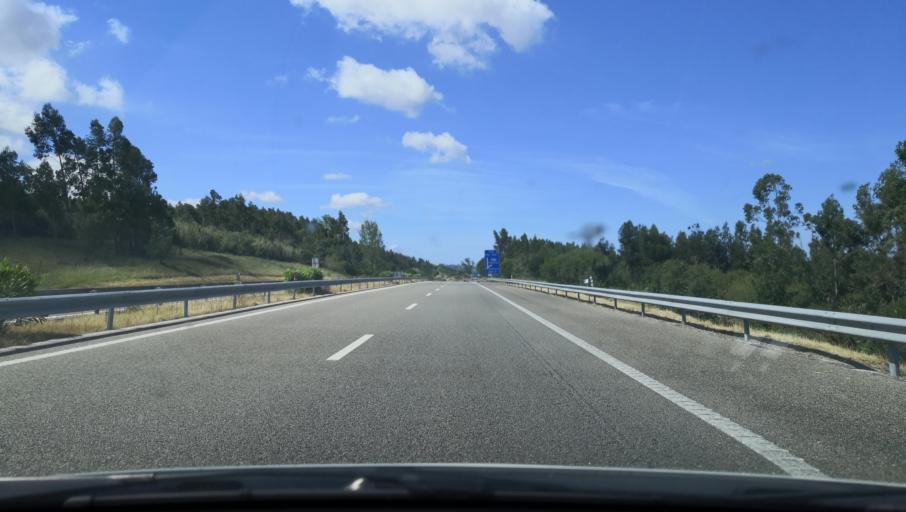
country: PT
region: Coimbra
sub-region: Montemor-O-Velho
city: Montemor-o-Velho
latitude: 40.1823
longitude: -8.7039
